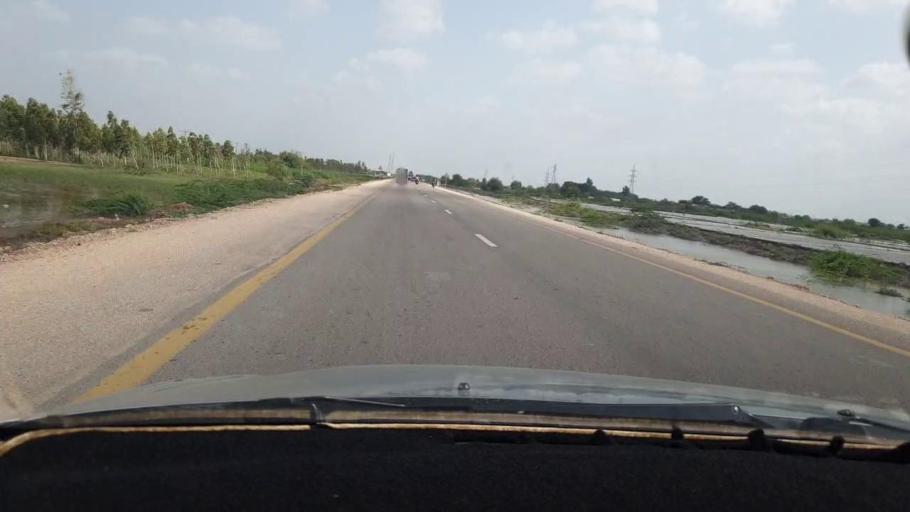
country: PK
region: Sindh
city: Digri
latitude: 25.0370
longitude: 69.2386
